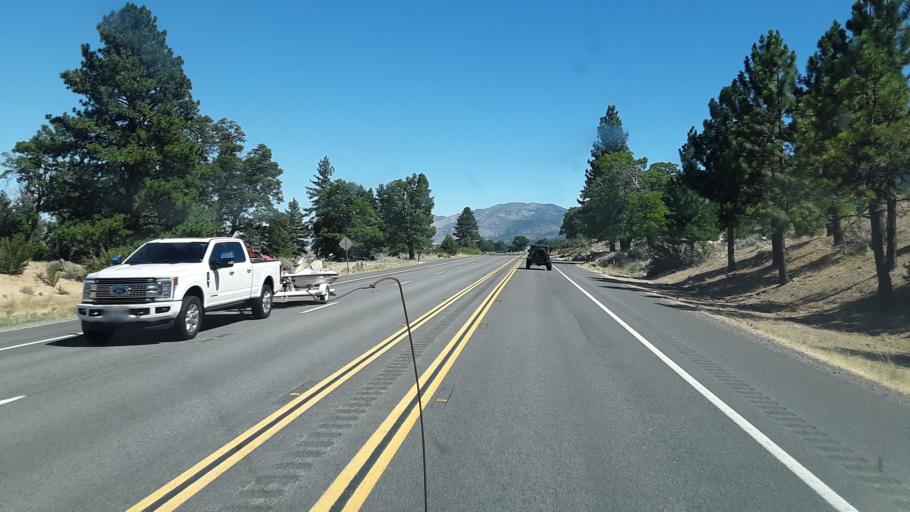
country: US
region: California
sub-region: Lassen County
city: Janesville
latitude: 40.2186
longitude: -120.4298
